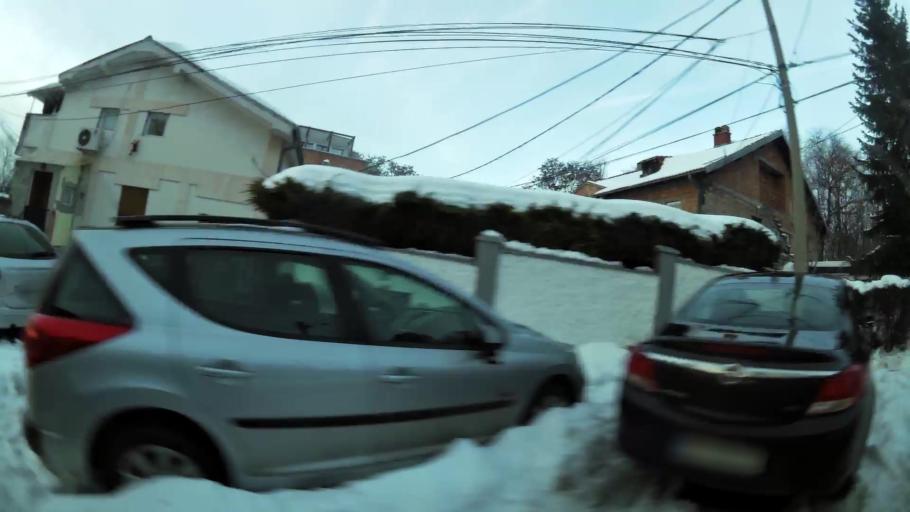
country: RS
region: Central Serbia
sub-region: Belgrade
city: Palilula
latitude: 44.7951
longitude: 20.5118
